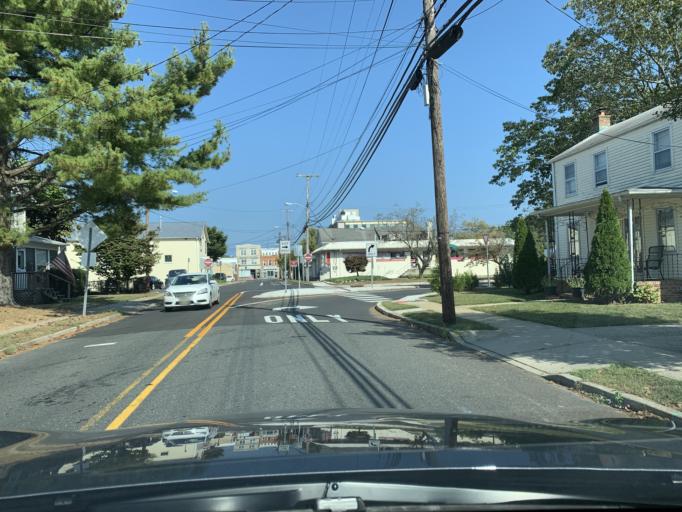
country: US
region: New Jersey
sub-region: Monmouth County
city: Eatontown
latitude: 40.3044
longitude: -74.0618
